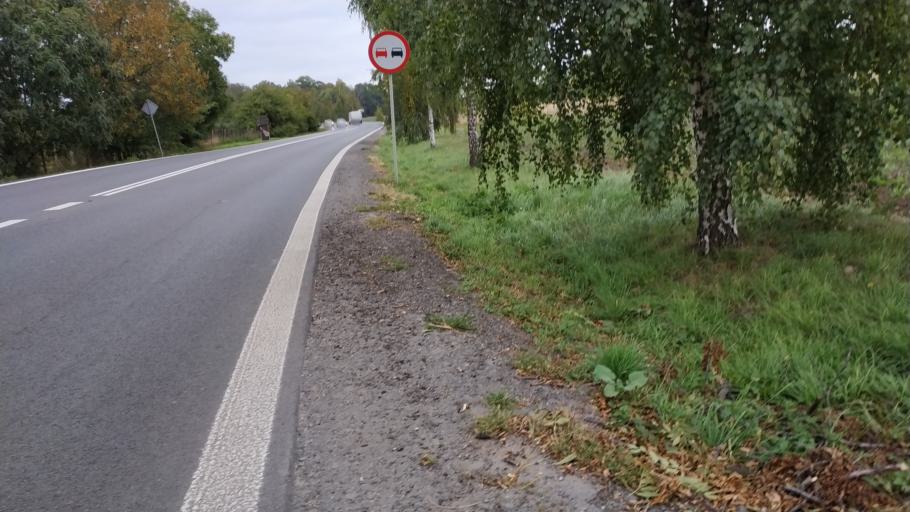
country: PL
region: Lower Silesian Voivodeship
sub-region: Powiat wroclawski
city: Tyniec Maly
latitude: 51.0237
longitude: 16.9256
